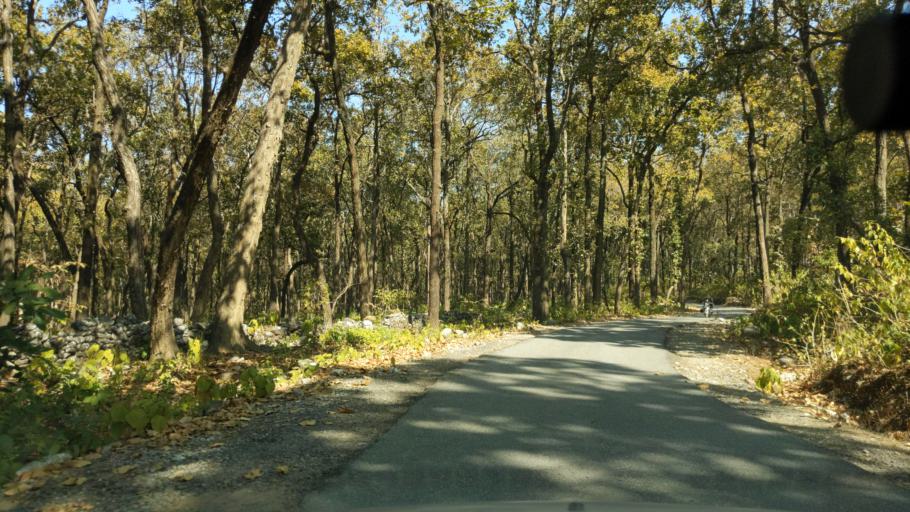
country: IN
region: Uttarakhand
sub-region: Naini Tal
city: Ramnagar
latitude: 29.4654
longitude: 79.2324
